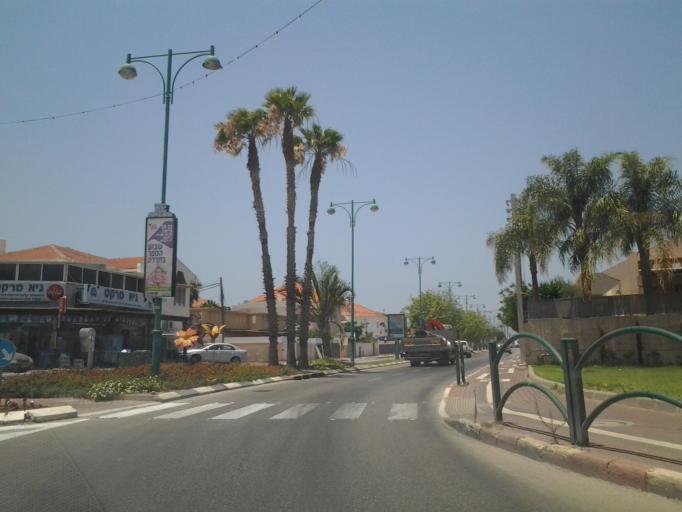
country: IL
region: Haifa
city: Hadera
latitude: 32.4462
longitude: 34.8985
